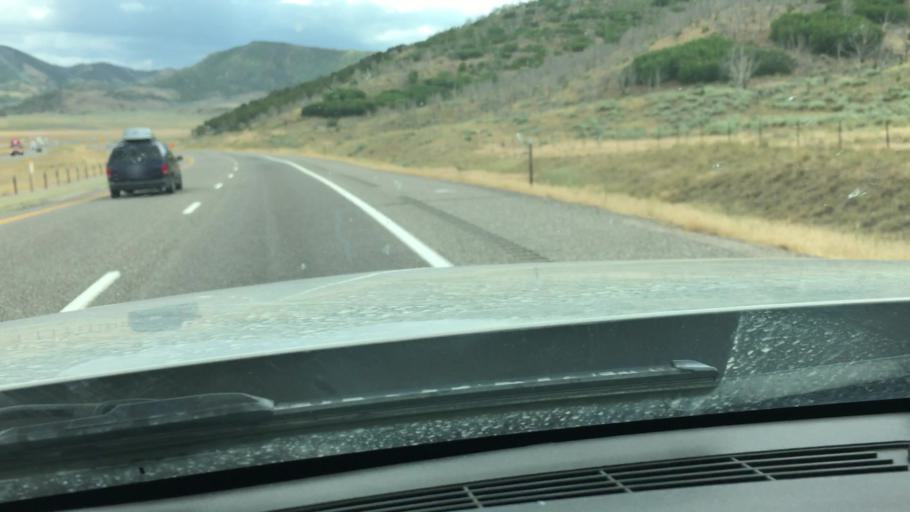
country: US
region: Utah
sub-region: Millard County
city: Fillmore
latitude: 38.6782
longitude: -112.5947
